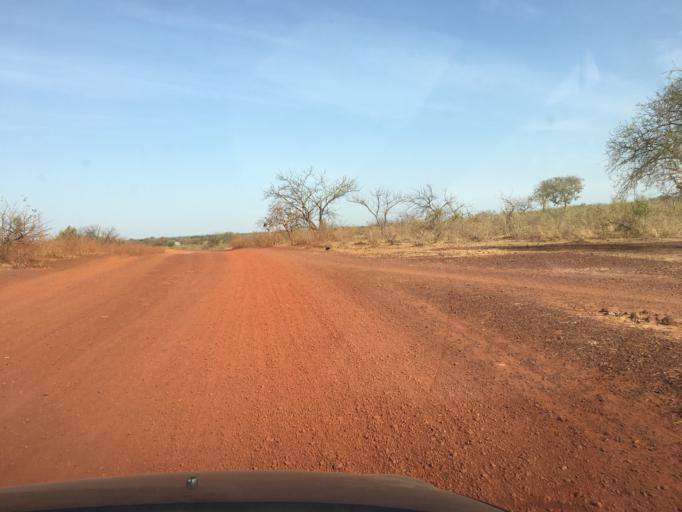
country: BF
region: Plateau-Central
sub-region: Province du Kourweogo
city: Bousse
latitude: 12.5618
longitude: -1.9021
